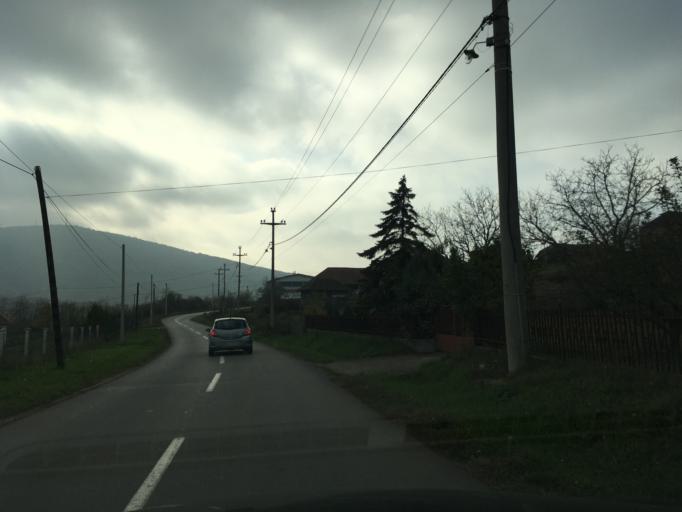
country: RS
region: Central Serbia
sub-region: Belgrade
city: Sopot
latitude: 44.4947
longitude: 20.5949
